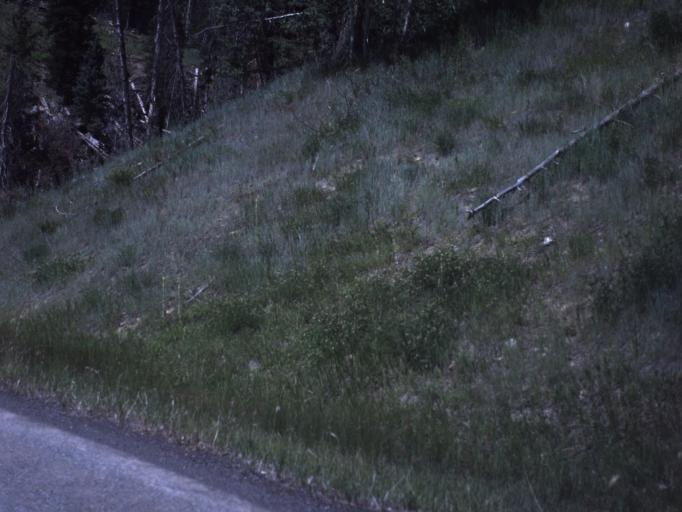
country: US
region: Utah
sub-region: Sanpete County
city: Fairview
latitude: 39.6786
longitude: -111.2149
